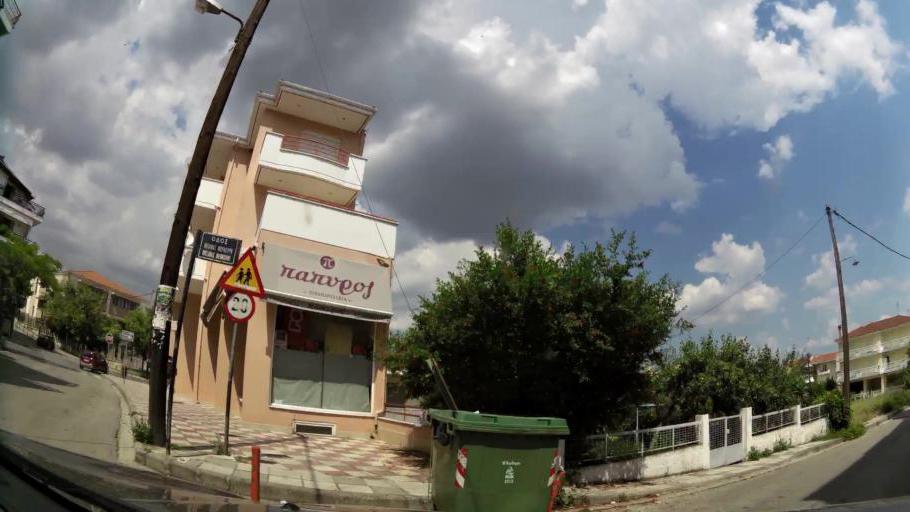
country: GR
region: West Macedonia
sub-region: Nomos Kozanis
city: Kozani
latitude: 40.3018
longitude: 21.7981
